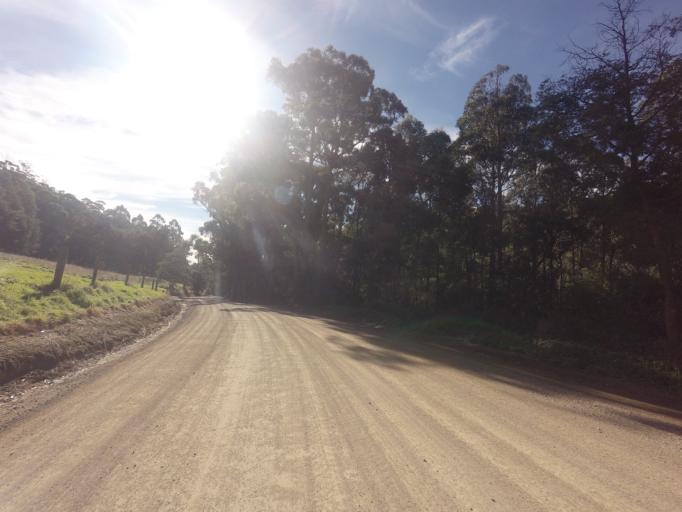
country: AU
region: Tasmania
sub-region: Clarence
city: Sandford
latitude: -43.1335
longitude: 147.7669
